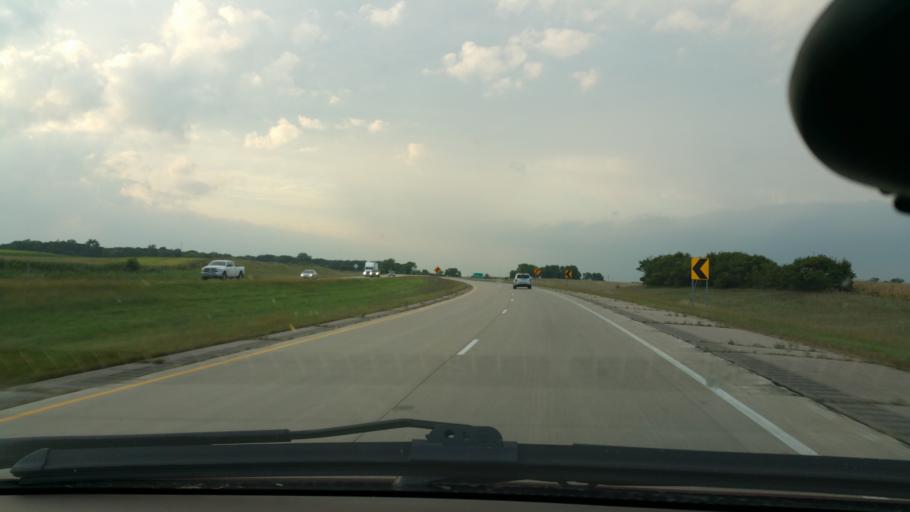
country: US
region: Minnesota
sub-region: Freeborn County
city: Albert Lea
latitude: 43.5448
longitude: -93.3554
